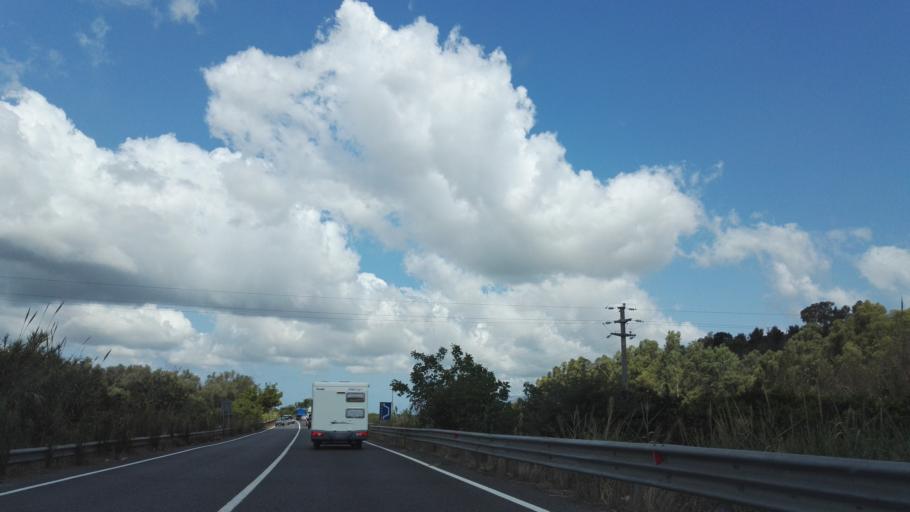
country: IT
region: Calabria
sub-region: Provincia di Reggio Calabria
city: Melicucco
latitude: 38.4496
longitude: 16.0350
